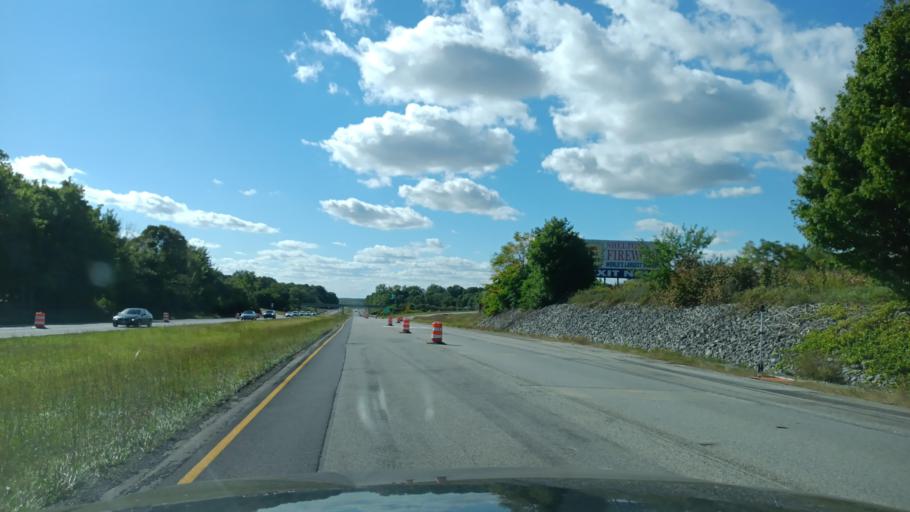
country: US
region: Indiana
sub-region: Fountain County
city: Covington
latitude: 40.1221
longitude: -87.3754
